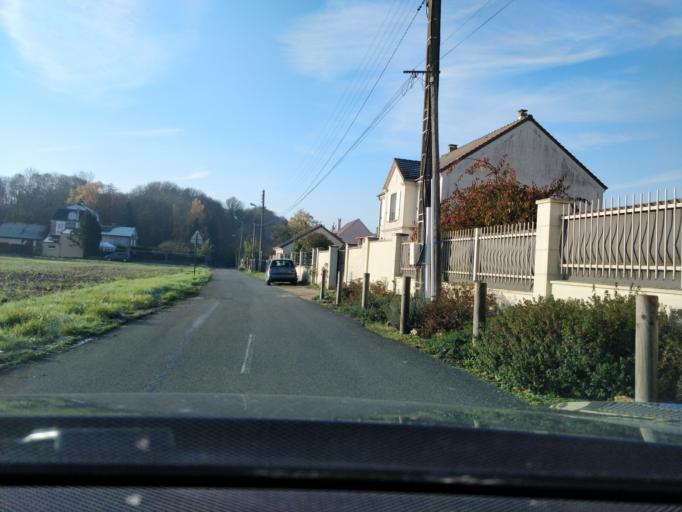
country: FR
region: Ile-de-France
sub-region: Departement de l'Essonne
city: Limours
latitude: 48.6531
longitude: 2.0856
